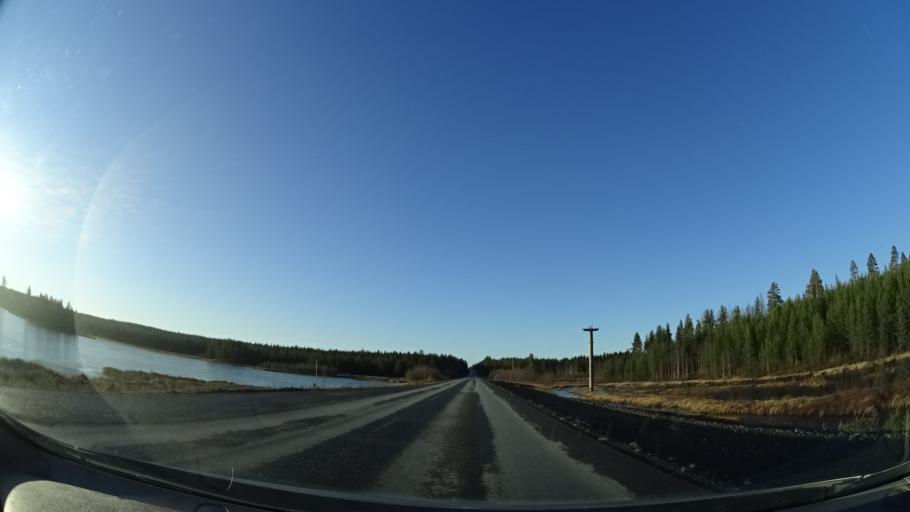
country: SE
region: Vaesterbotten
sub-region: Skelleftea Kommun
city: Langsele
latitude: 64.8850
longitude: 20.2915
